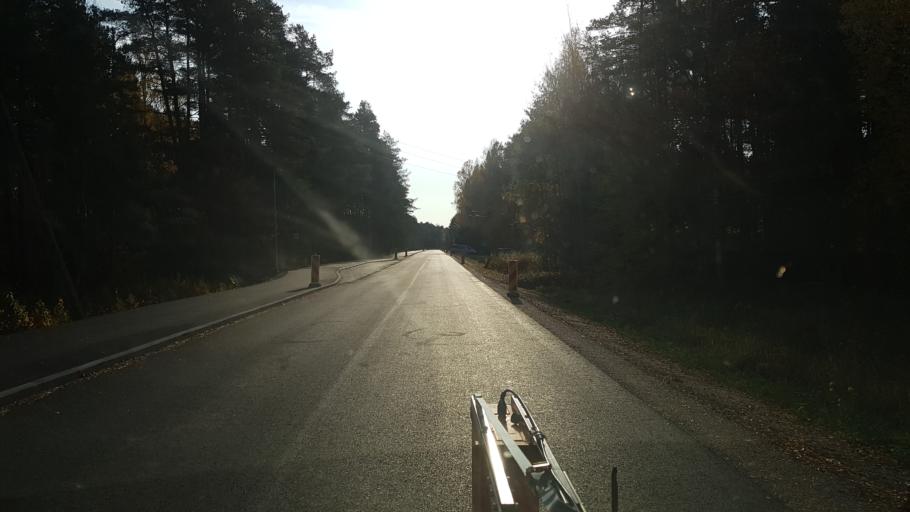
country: EE
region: Paernumaa
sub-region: Paikuse vald
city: Paikuse
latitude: 58.3581
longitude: 24.6128
